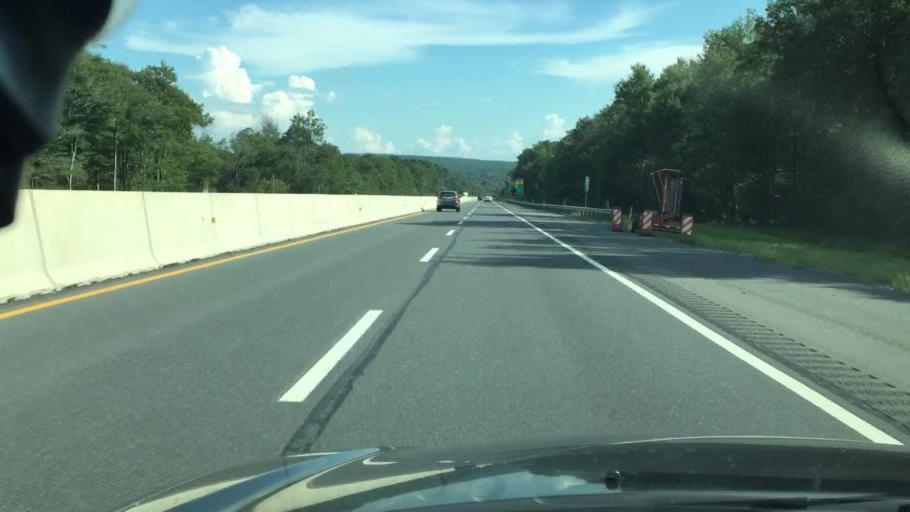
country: US
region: Pennsylvania
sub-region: Carbon County
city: Towamensing Trails
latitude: 41.0201
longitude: -75.6441
